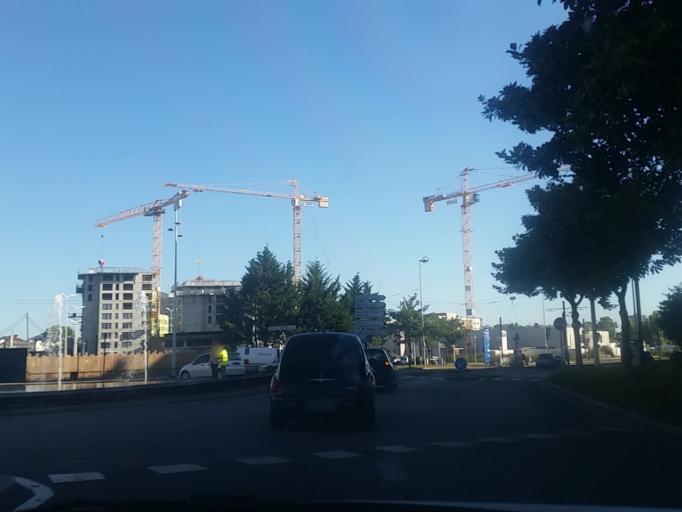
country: FR
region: Pays de la Loire
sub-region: Departement de la Loire-Atlantique
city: Reze
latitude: 47.1913
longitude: -1.5479
